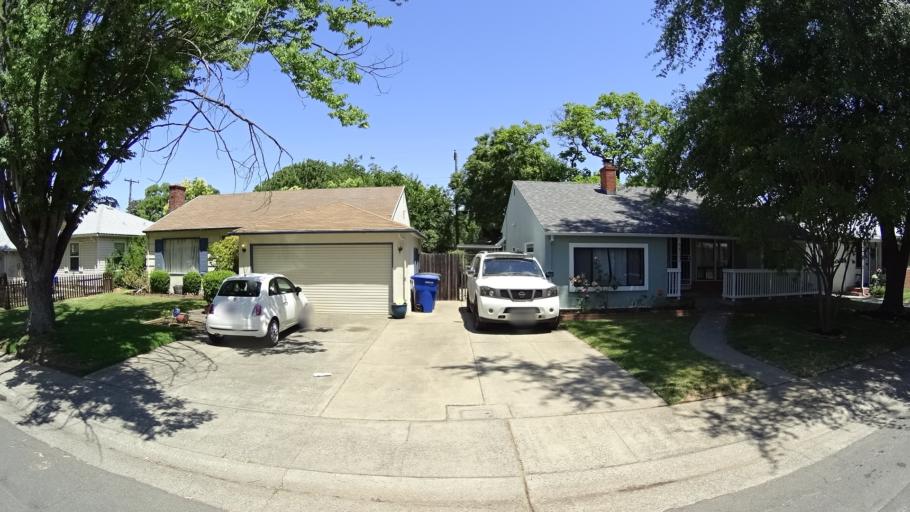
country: US
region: California
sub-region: Sacramento County
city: Parkway
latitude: 38.5409
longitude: -121.4369
